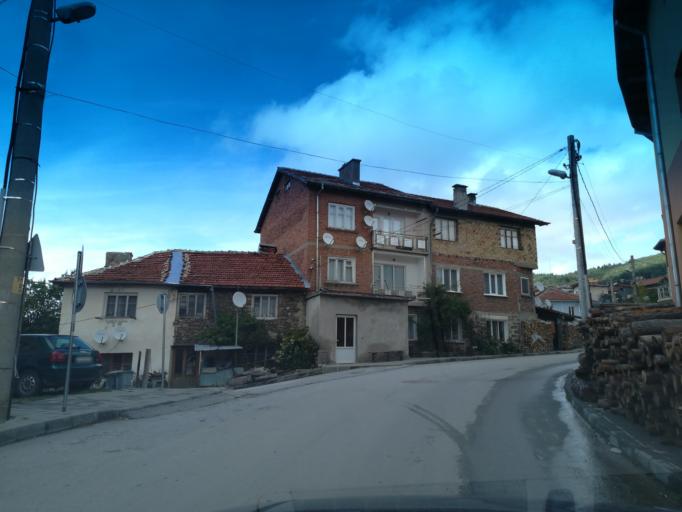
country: BG
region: Pazardzhik
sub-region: Obshtina Batak
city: Batak
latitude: 41.9381
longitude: 24.2710
